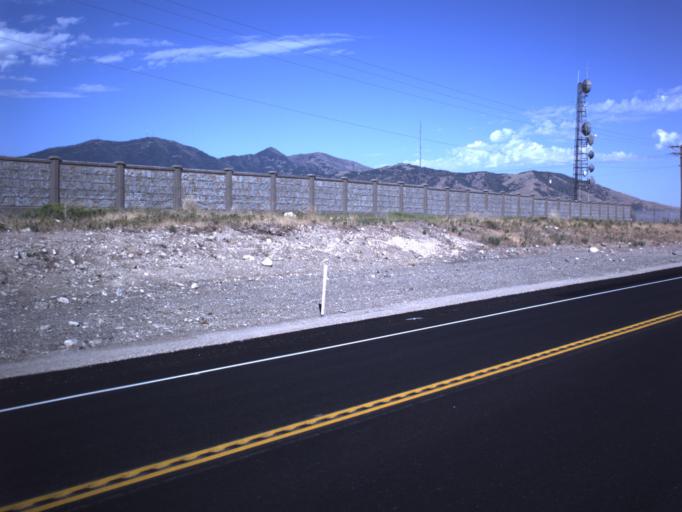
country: US
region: Utah
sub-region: Salt Lake County
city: Oquirrh
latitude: 40.6343
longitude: -112.0549
